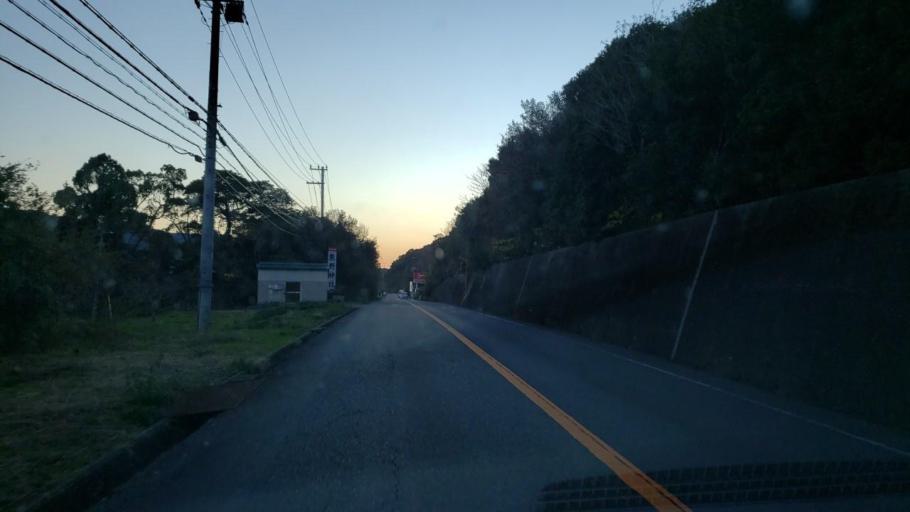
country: JP
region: Hyogo
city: Fukura
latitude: 34.3008
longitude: 134.7346
